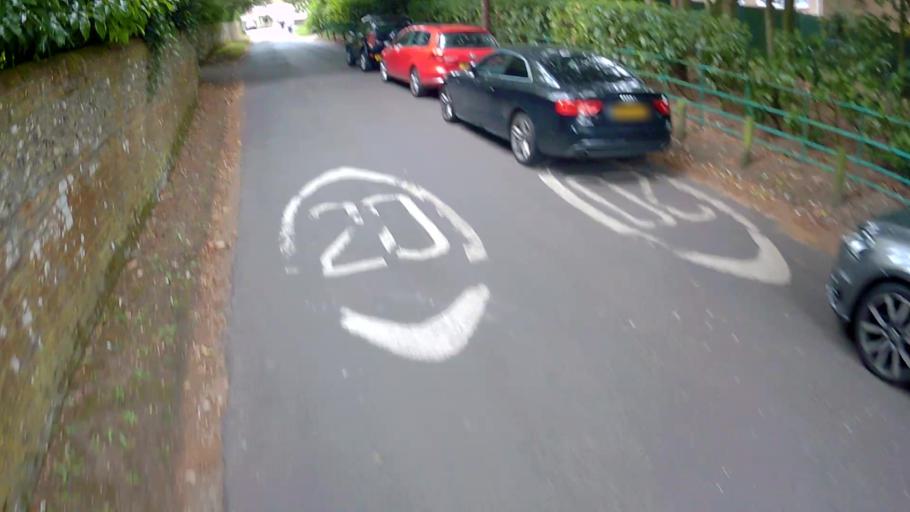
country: GB
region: England
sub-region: Hampshire
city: Basingstoke
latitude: 51.2114
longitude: -1.1596
